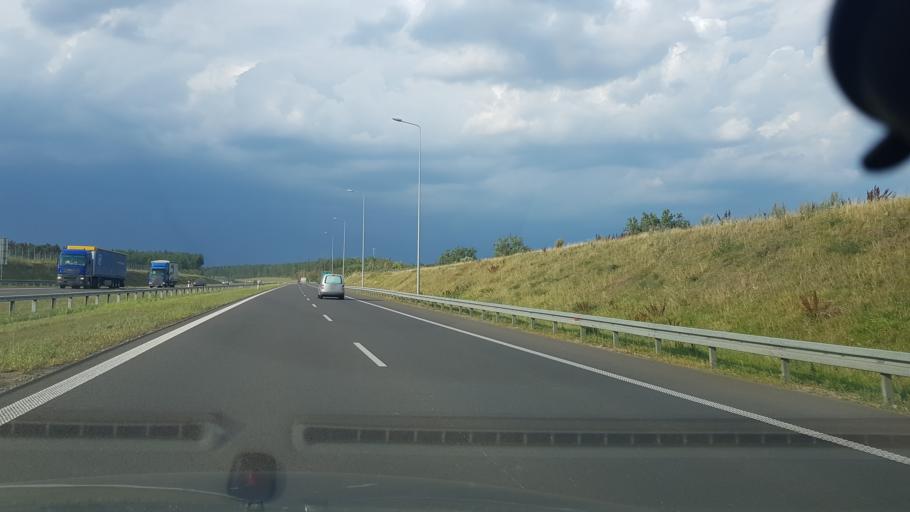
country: PL
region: Masovian Voivodeship
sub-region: Powiat mlawski
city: Wieczfnia Koscielna
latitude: 53.2333
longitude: 20.4203
